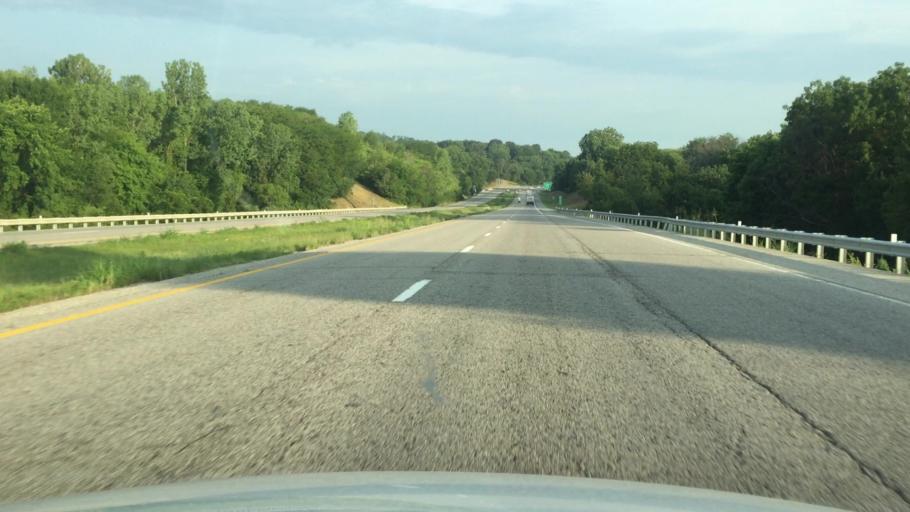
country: US
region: Missouri
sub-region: Buchanan County
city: Saint Joseph
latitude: 39.7242
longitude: -94.8381
